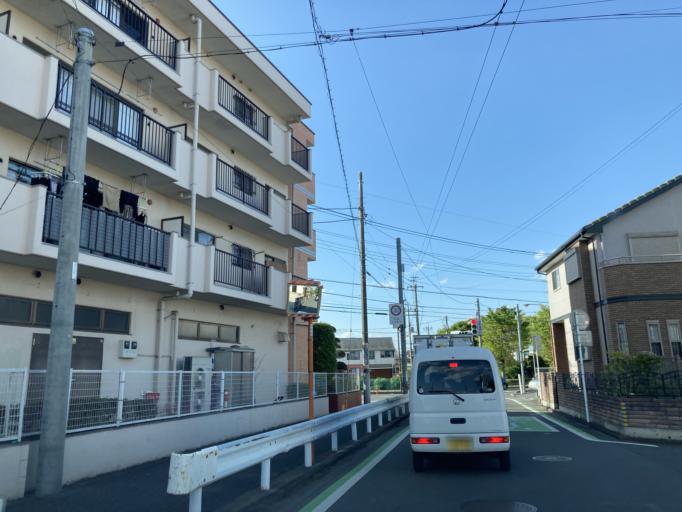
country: JP
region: Saitama
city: Sayama
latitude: 35.8704
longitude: 139.4364
